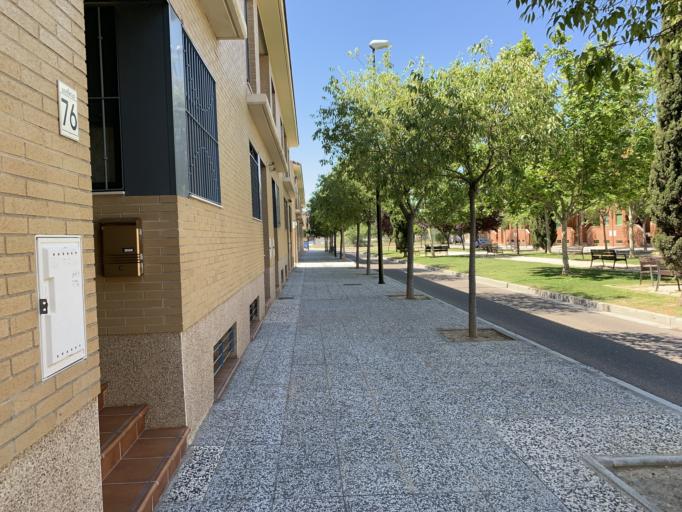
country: ES
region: Aragon
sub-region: Provincia de Zaragoza
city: Zaragoza
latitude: 41.6716
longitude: -0.8318
